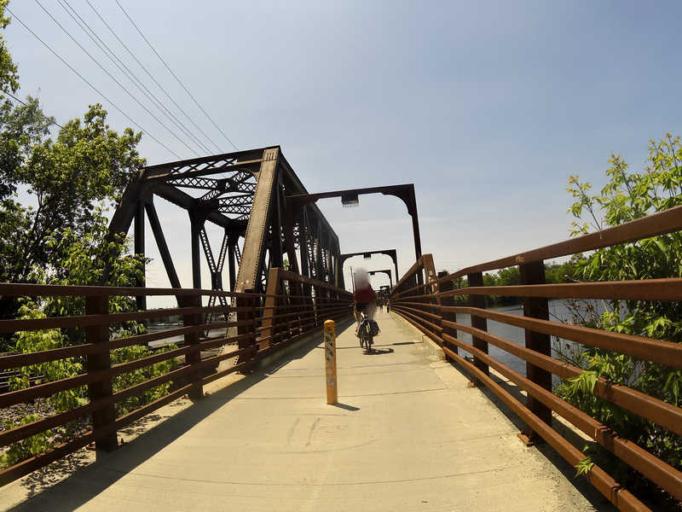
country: CA
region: Ontario
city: Peterborough
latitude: 44.2997
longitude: -78.3156
